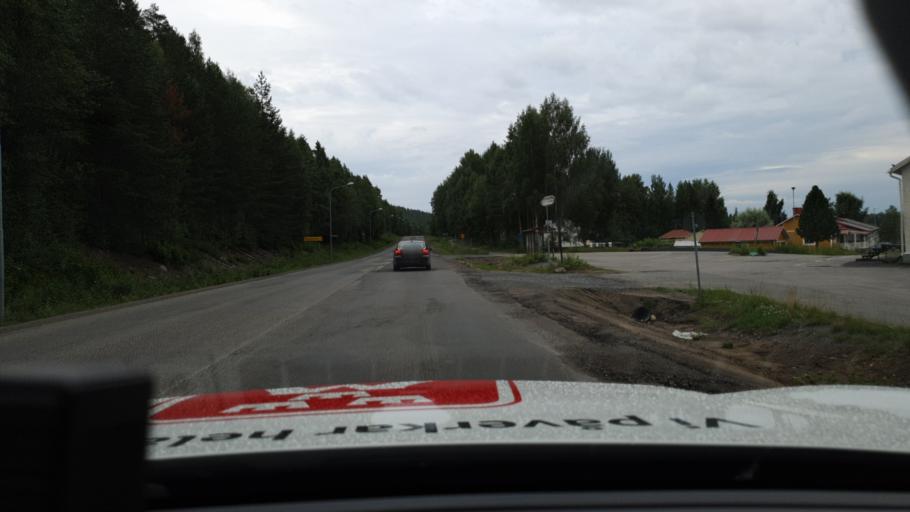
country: SE
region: Norrbotten
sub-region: Bodens Kommun
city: Boden
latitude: 65.8443
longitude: 21.6008
